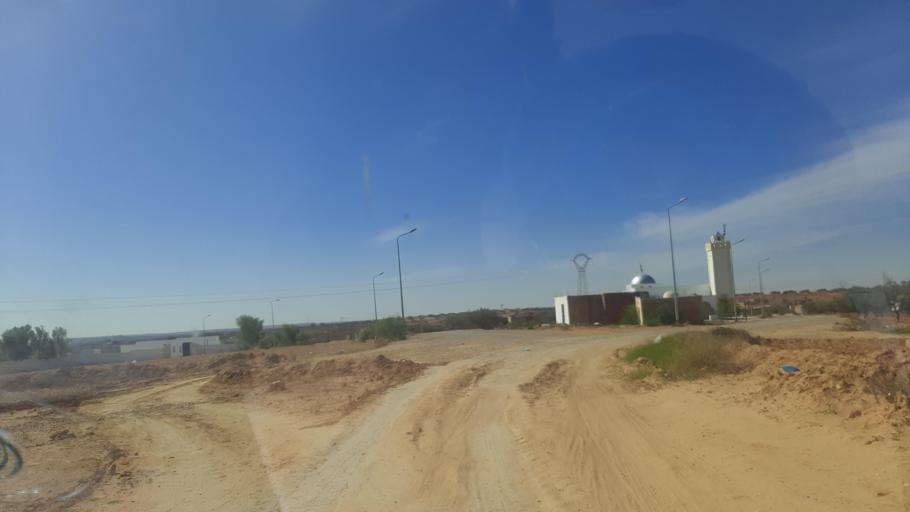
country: TN
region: Safaqis
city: Sfax
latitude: 34.7896
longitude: 10.5309
